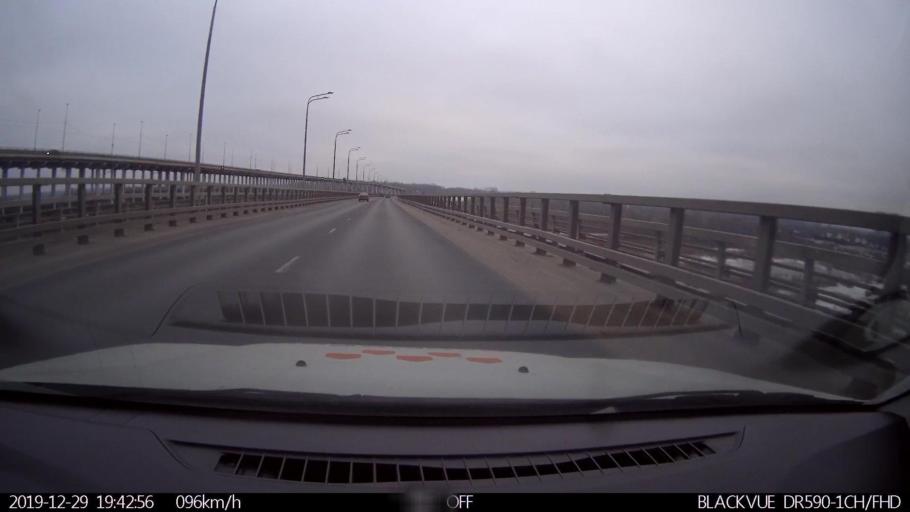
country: RU
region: Nizjnij Novgorod
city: Neklyudovo
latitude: 56.3562
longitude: 43.9278
